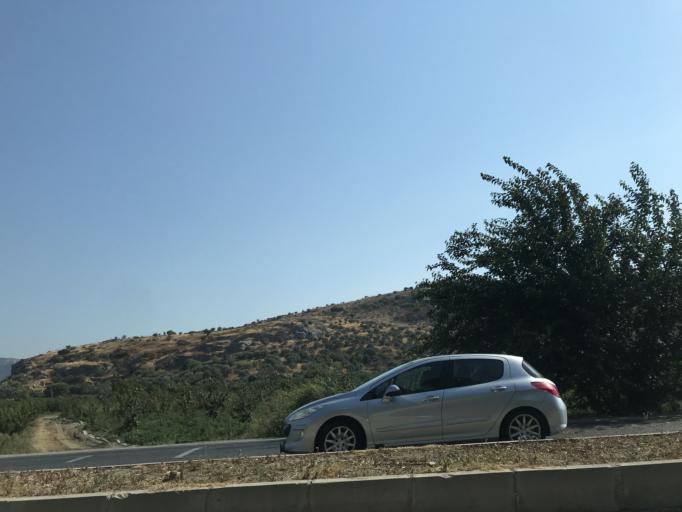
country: TR
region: Izmir
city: Selcuk
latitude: 37.9500
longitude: 27.3521
